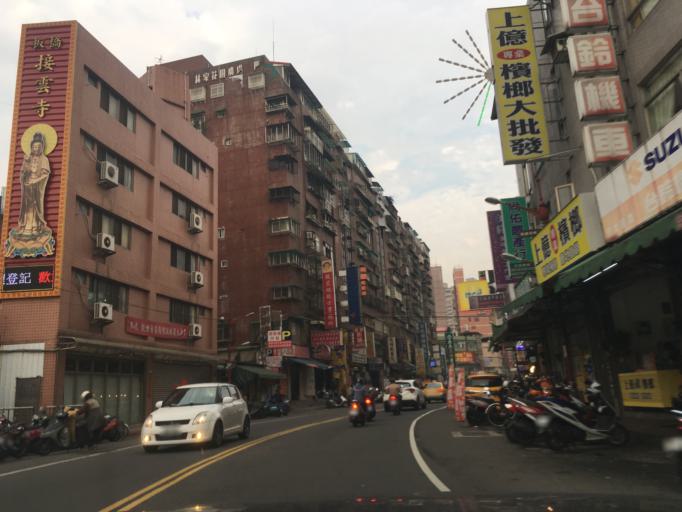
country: TW
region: Taipei
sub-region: Taipei
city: Banqiao
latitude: 25.0086
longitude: 121.4543
